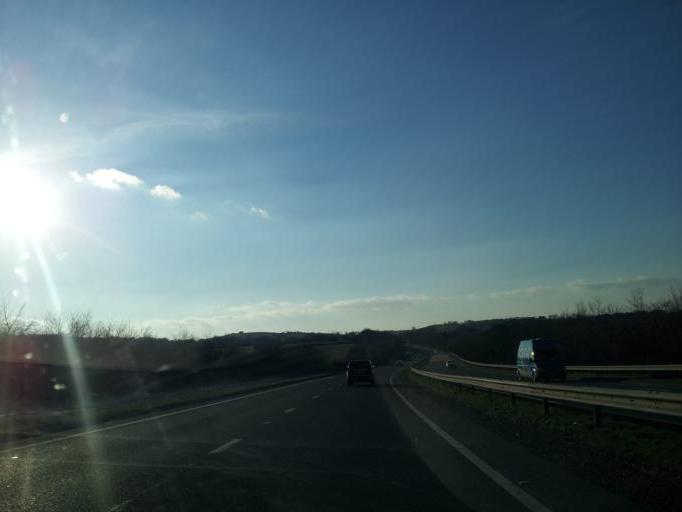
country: GB
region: England
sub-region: Devon
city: Okehampton
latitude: 50.7395
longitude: -3.9145
